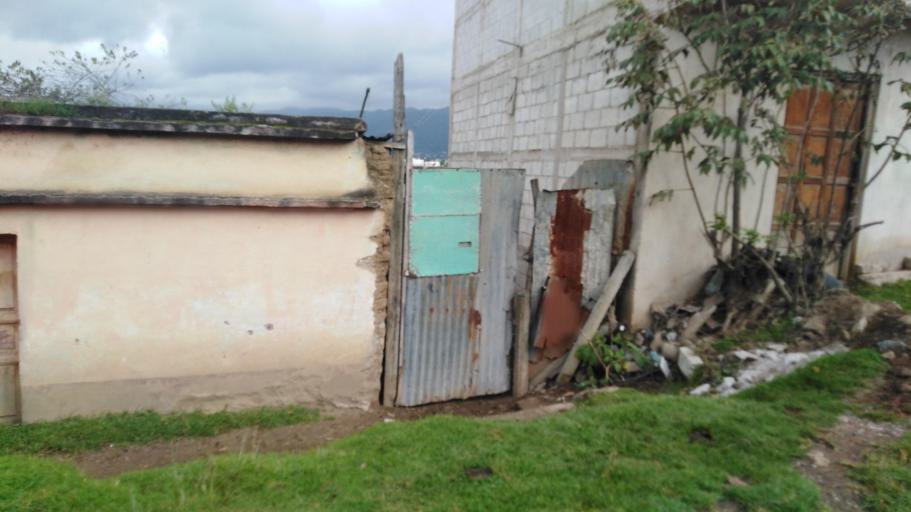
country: GT
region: Quetzaltenango
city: Olintepeque
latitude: 14.8638
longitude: -91.5004
